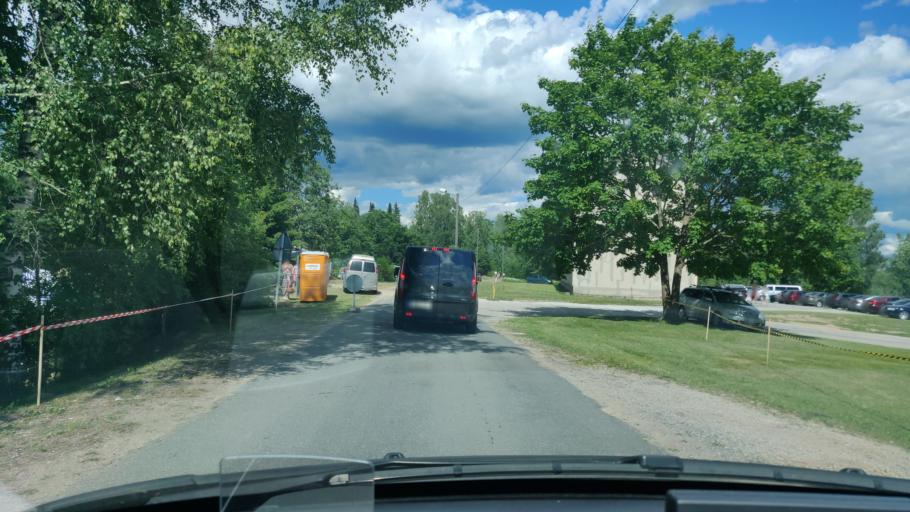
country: EE
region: Jogevamaa
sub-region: Mustvee linn
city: Mustvee
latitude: 58.9852
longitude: 26.8729
